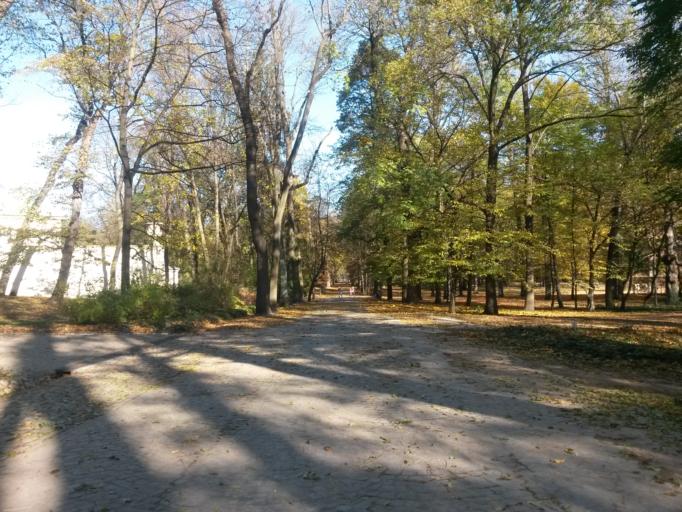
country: PL
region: Masovian Voivodeship
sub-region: Warszawa
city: Srodmiescie
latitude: 52.2153
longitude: 21.0303
